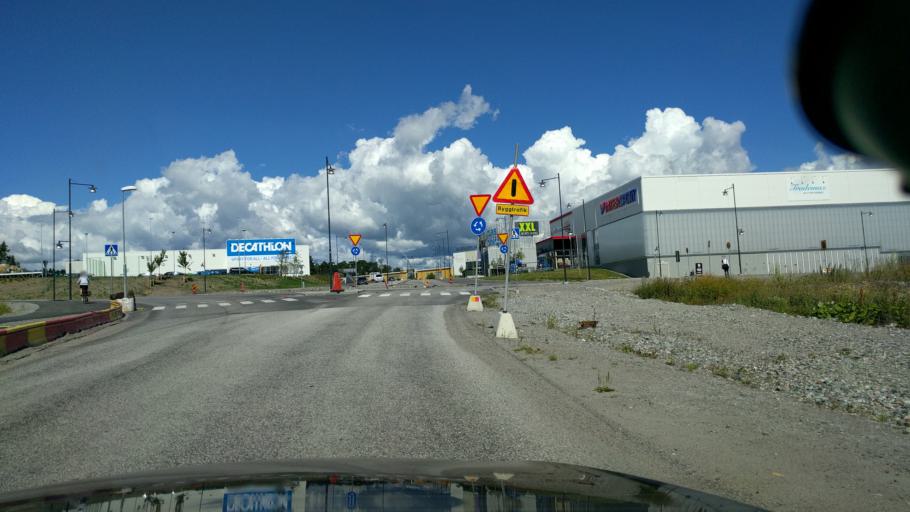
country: SE
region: Stockholm
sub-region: Jarfalla Kommun
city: Jakobsberg
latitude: 59.4104
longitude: 17.8616
